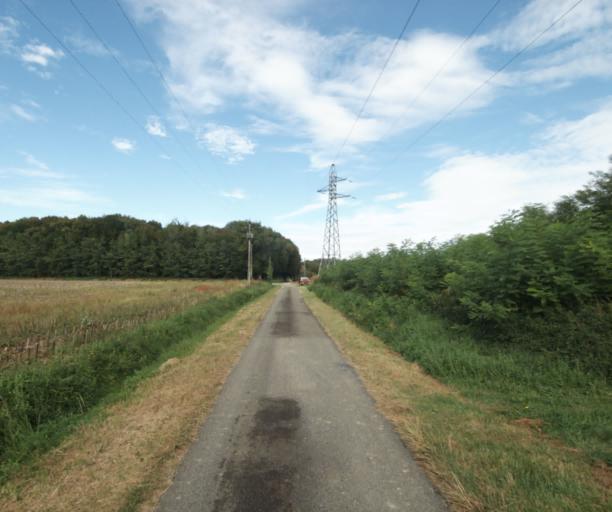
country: FR
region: Aquitaine
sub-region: Departement des Landes
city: Villeneuve-de-Marsan
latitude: 43.9059
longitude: -0.2248
